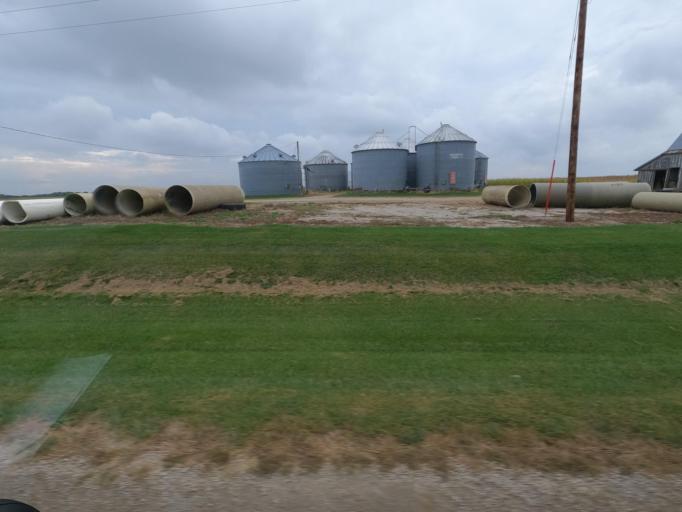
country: US
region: Iowa
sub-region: Van Buren County
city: Keosauqua
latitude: 40.8135
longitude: -91.8726
